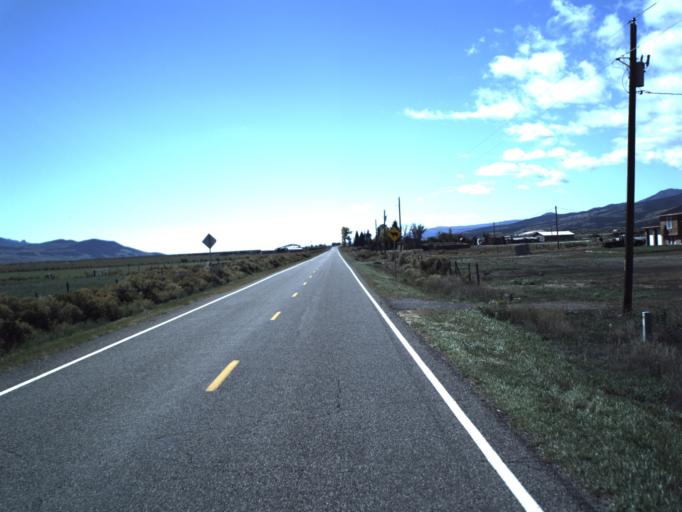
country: US
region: Utah
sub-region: Sevier County
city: Monroe
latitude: 38.4549
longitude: -111.9121
